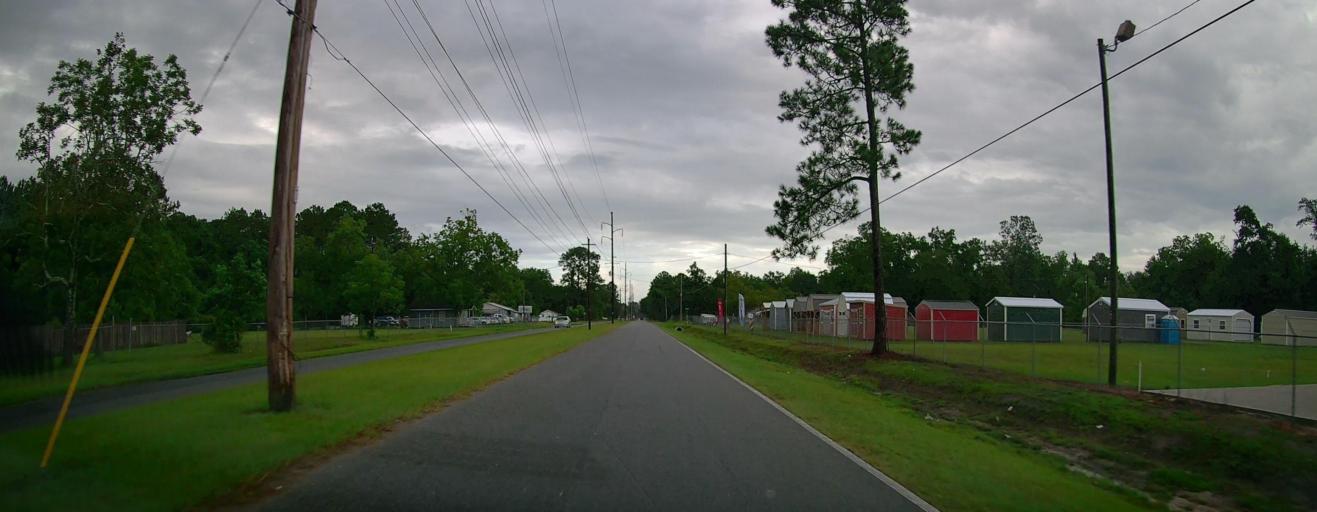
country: US
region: Georgia
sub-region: Ware County
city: Deenwood
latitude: 31.2148
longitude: -82.3882
